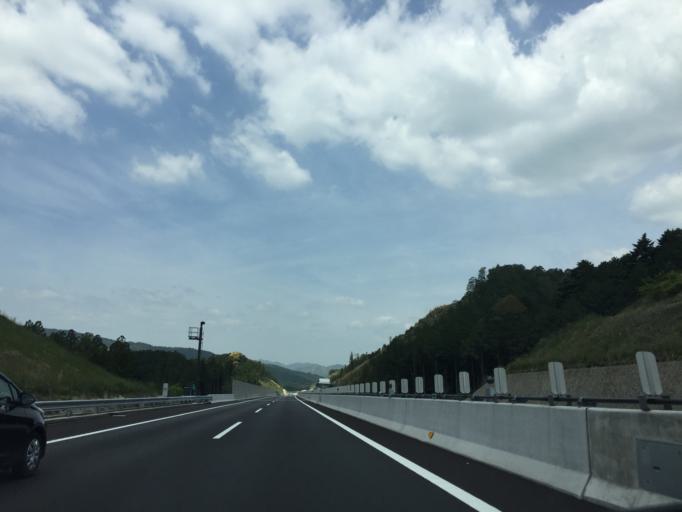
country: JP
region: Aichi
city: Shinshiro
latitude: 34.9004
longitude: 137.6208
